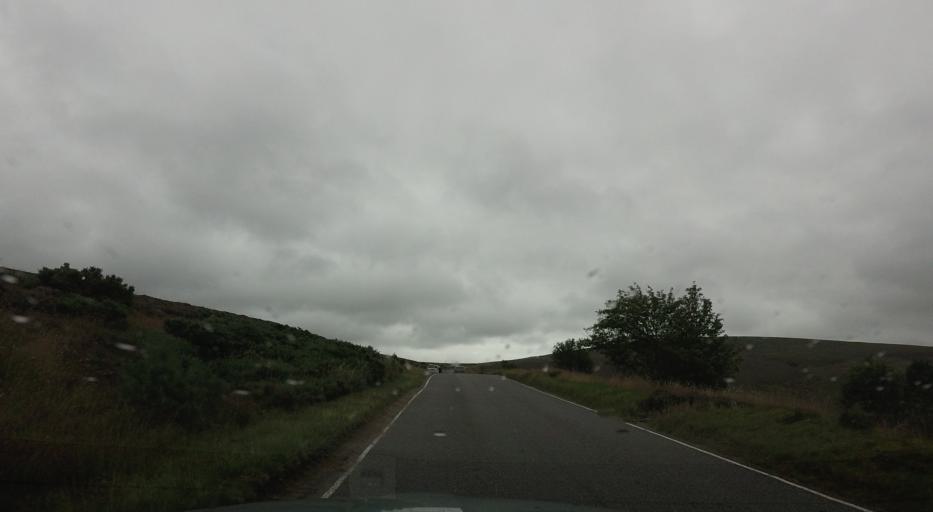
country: GB
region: Scotland
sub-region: Aberdeenshire
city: Banchory
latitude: 56.9456
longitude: -2.5784
